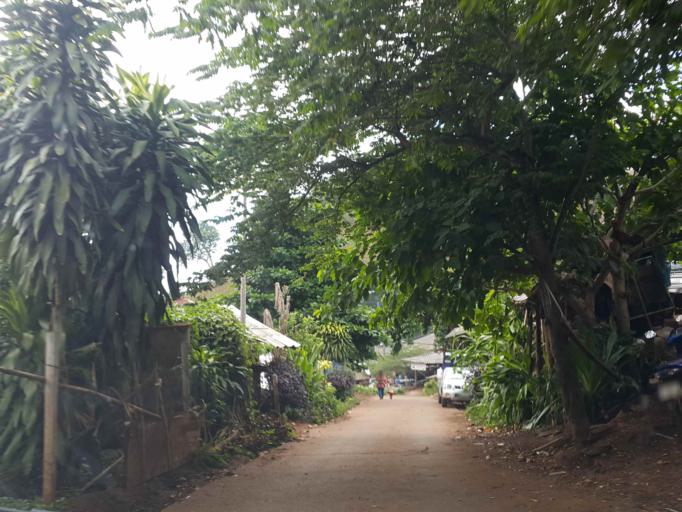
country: TH
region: Chiang Mai
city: Samoeng
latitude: 18.7822
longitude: 98.8261
